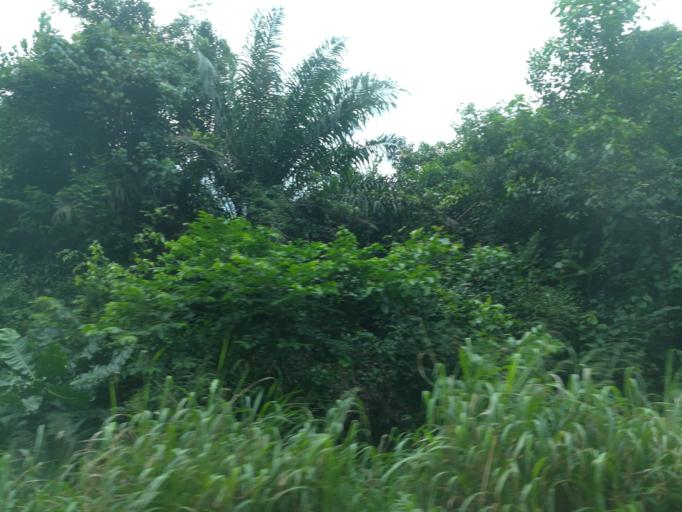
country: NG
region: Lagos
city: Ejirin
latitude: 6.6458
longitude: 3.7234
